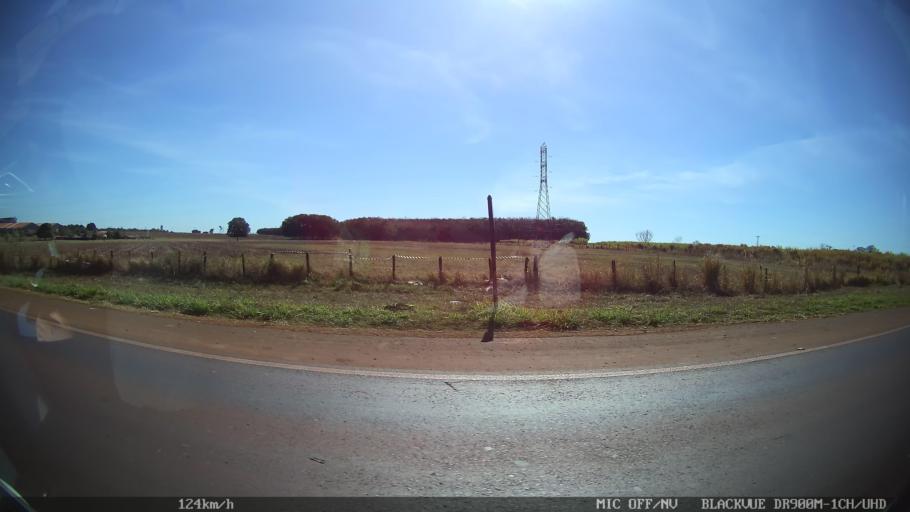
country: BR
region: Sao Paulo
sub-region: Barretos
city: Barretos
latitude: -20.5087
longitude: -48.5559
